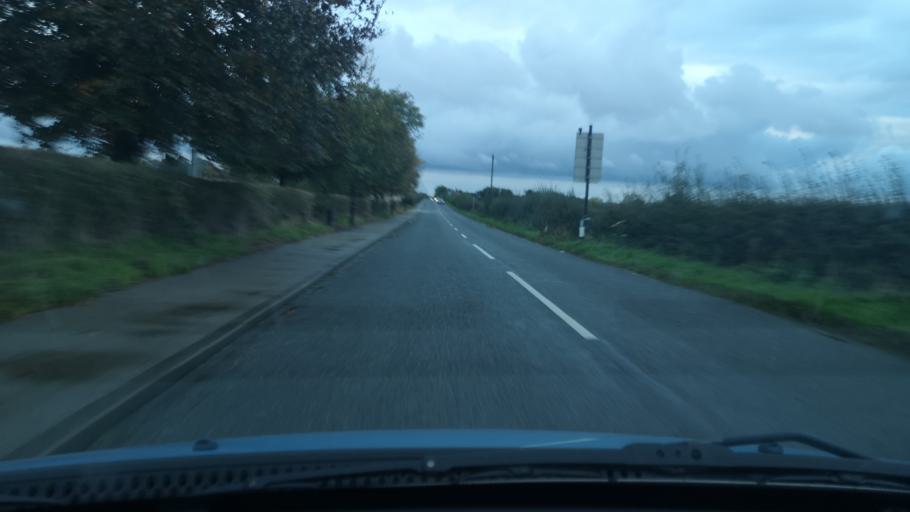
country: GB
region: England
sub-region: Doncaster
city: Campsall
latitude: 53.6259
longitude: -1.1815
